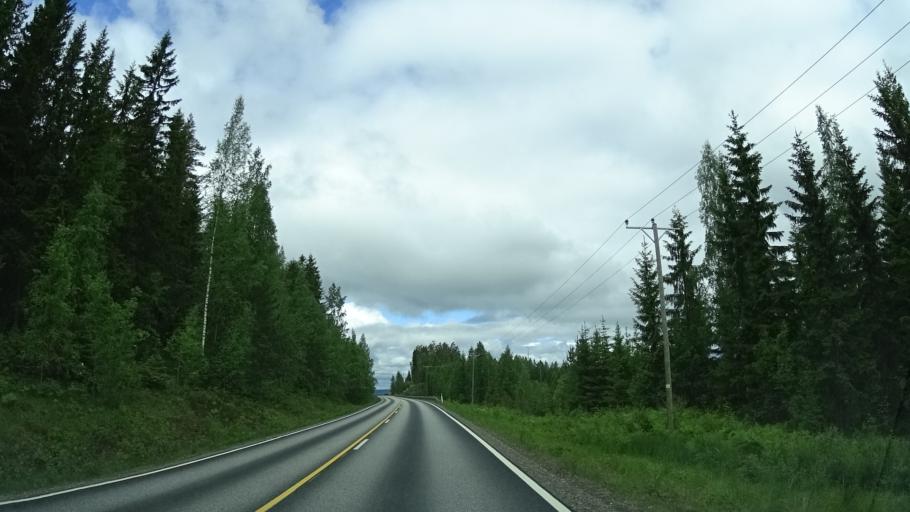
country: FI
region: Central Finland
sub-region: Joutsa
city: Luhanka
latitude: 61.9368
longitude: 25.7209
